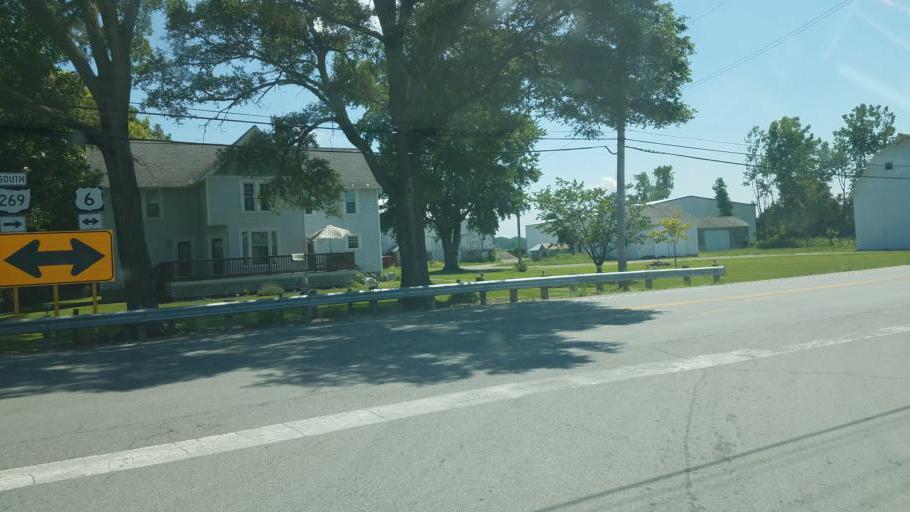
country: US
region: Ohio
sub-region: Erie County
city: Sandusky
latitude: 41.4418
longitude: -82.8131
